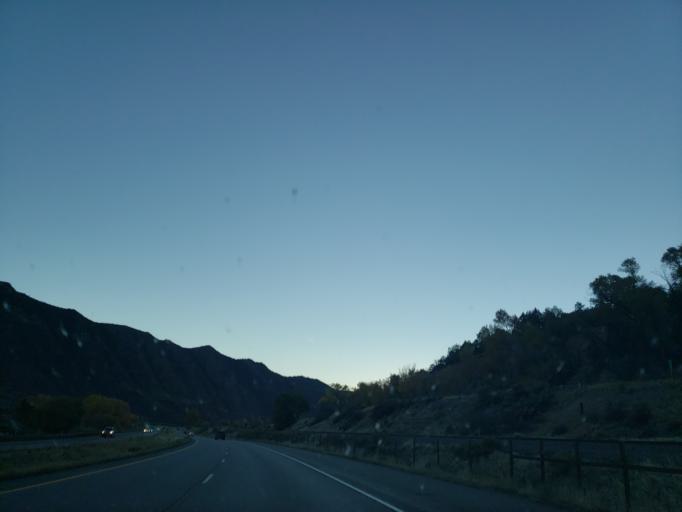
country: US
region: Colorado
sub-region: Garfield County
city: New Castle
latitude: 39.5713
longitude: -107.4823
